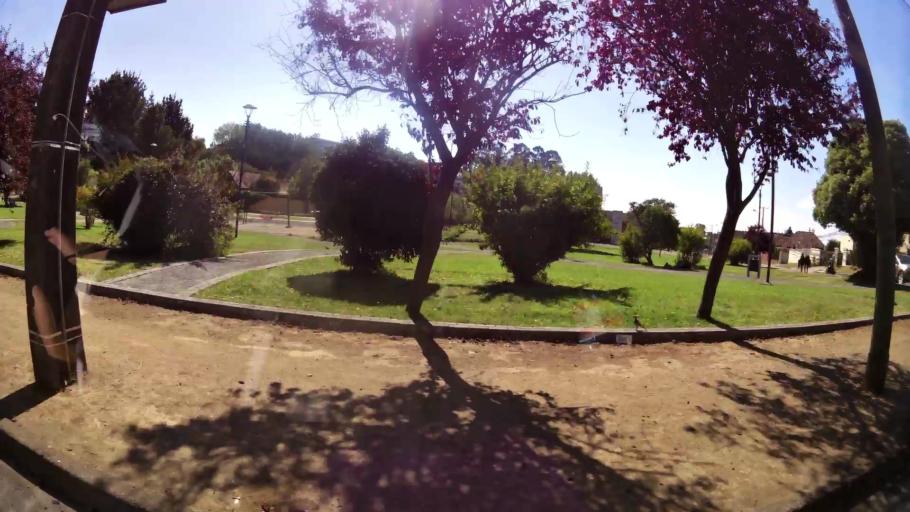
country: CL
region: Biobio
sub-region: Provincia de Concepcion
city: Concepcion
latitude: -36.7921
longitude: -73.0574
